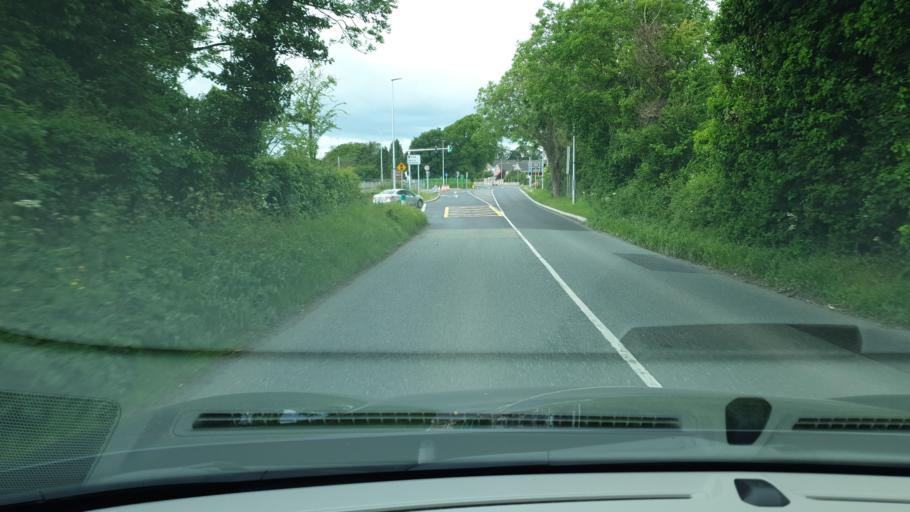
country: IE
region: Leinster
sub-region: An Mhi
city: Ratoath
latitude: 53.5033
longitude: -6.4438
